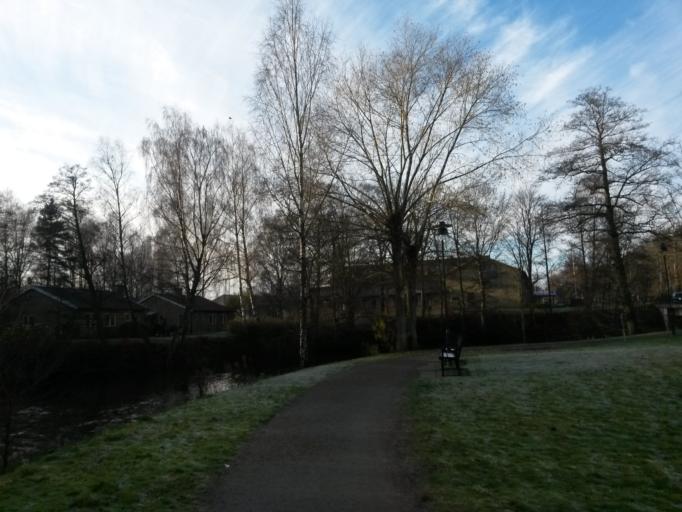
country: SE
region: Vaestra Goetaland
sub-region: Alingsas Kommun
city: Alingsas
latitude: 57.9320
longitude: 12.5265
